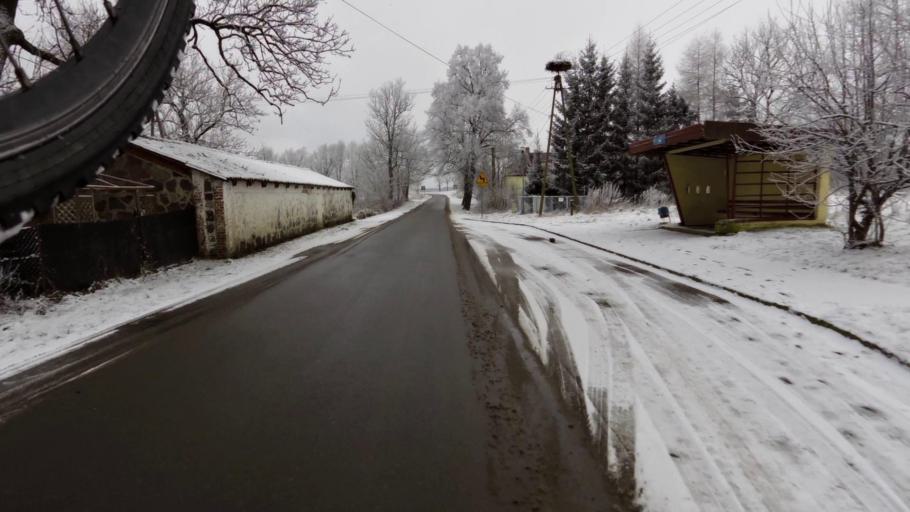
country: PL
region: West Pomeranian Voivodeship
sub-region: Powiat swidwinski
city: Rabino
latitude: 53.8335
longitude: 15.9407
